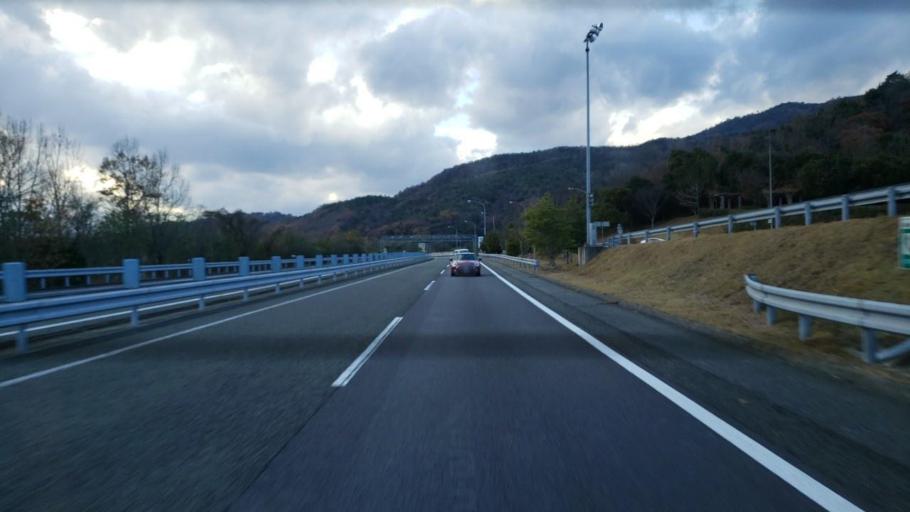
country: JP
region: Tokushima
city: Ishii
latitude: 34.1399
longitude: 134.4101
